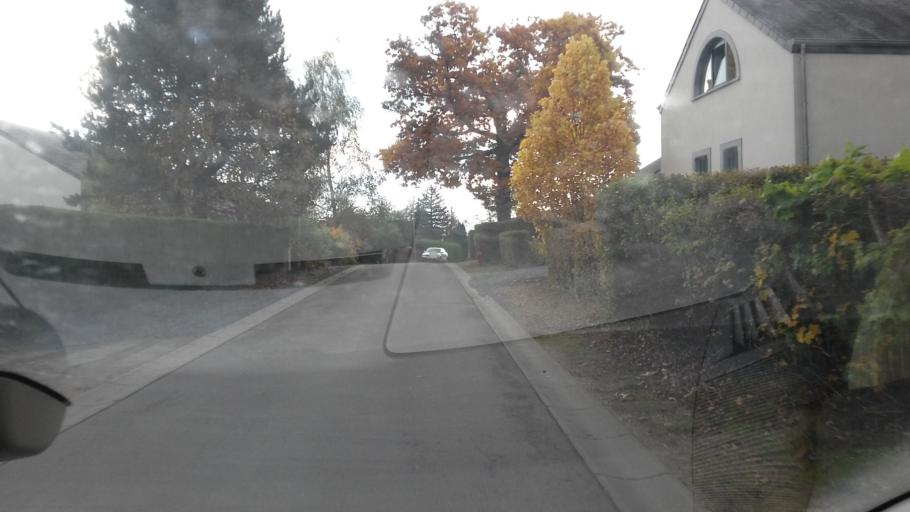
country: BE
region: Wallonia
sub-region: Province du Luxembourg
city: Arlon
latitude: 49.6784
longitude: 5.8266
